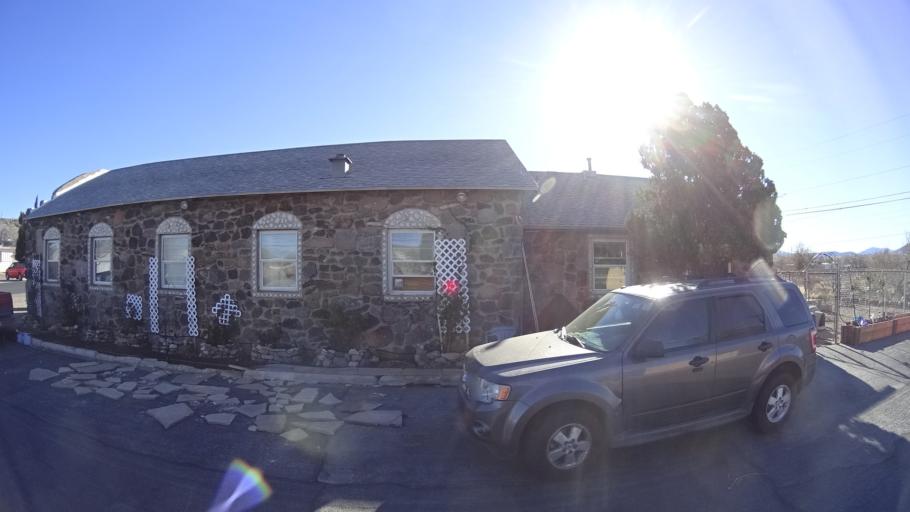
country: US
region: Arizona
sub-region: Mohave County
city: Kingman
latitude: 35.1863
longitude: -114.0517
